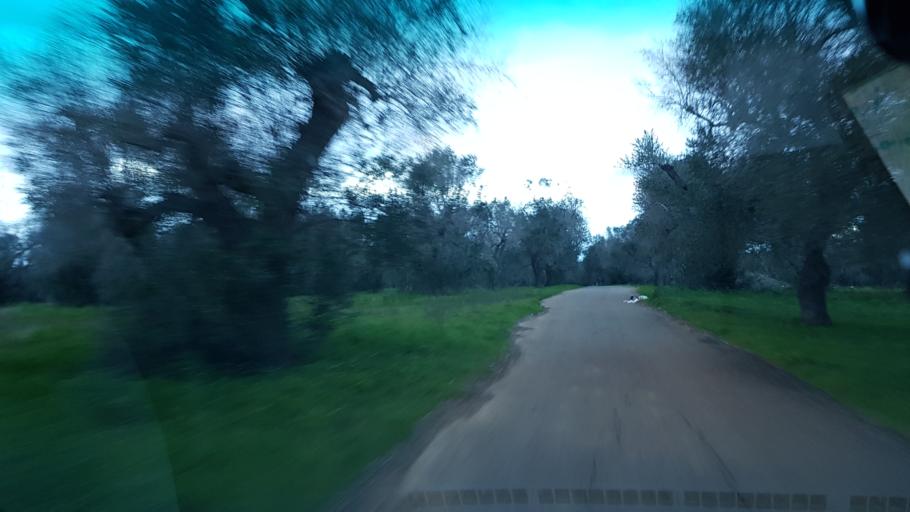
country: IT
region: Apulia
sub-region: Provincia di Brindisi
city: Torchiarolo
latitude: 40.4902
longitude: 18.0586
